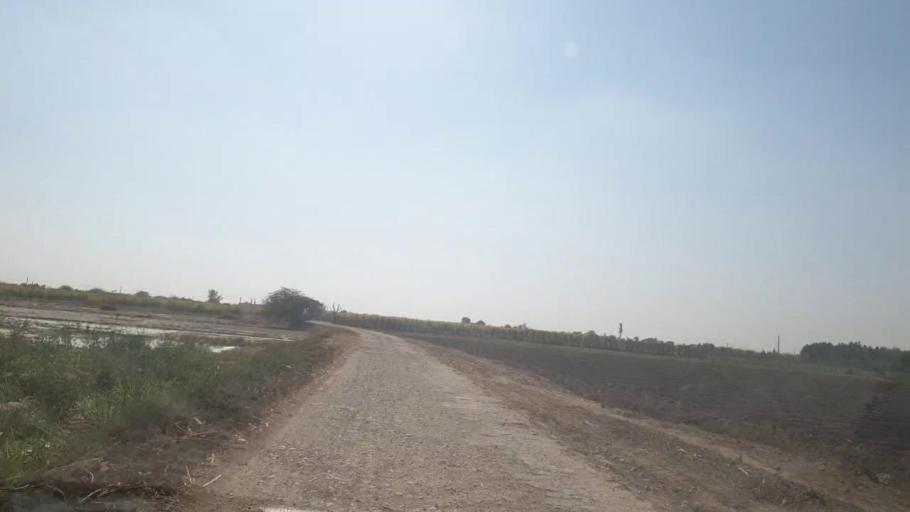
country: PK
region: Sindh
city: Mirpur Khas
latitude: 25.4752
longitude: 69.1276
